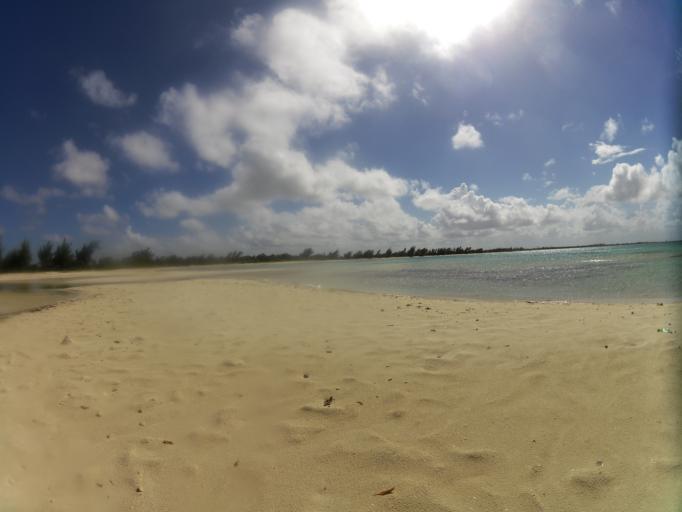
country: CU
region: Las Tunas
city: Puerto Padre
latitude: 21.2768
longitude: -76.5196
